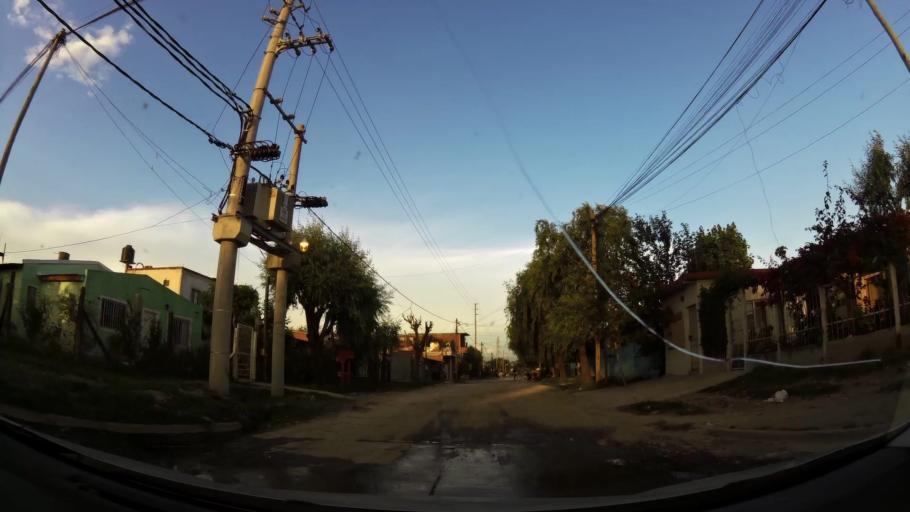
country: AR
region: Buenos Aires
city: Santa Catalina - Dique Lujan
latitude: -34.4310
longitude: -58.6634
